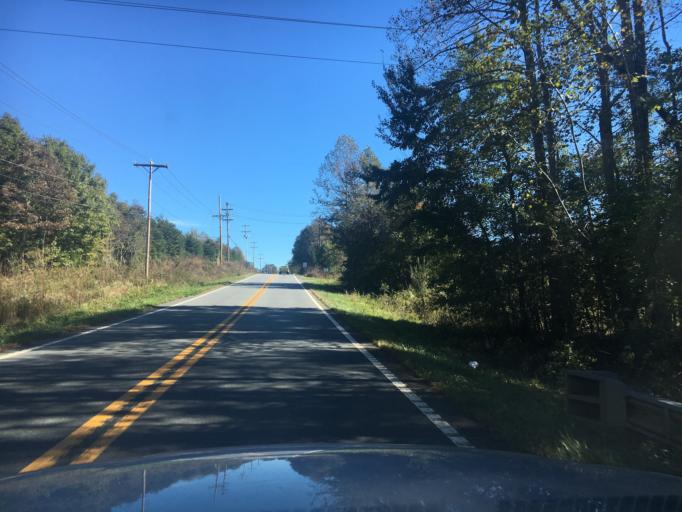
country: US
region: North Carolina
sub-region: Rutherford County
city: Spindale
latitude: 35.4123
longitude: -81.9192
